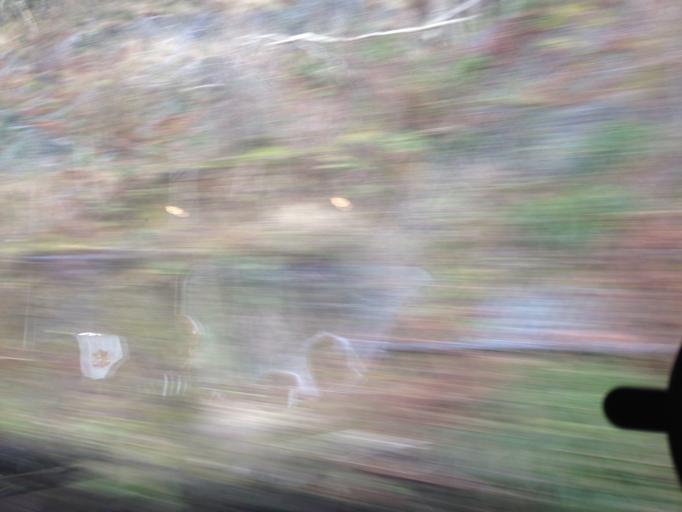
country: GB
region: Scotland
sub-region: Argyll and Bute
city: Garelochhead
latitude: 56.1811
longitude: -4.7710
